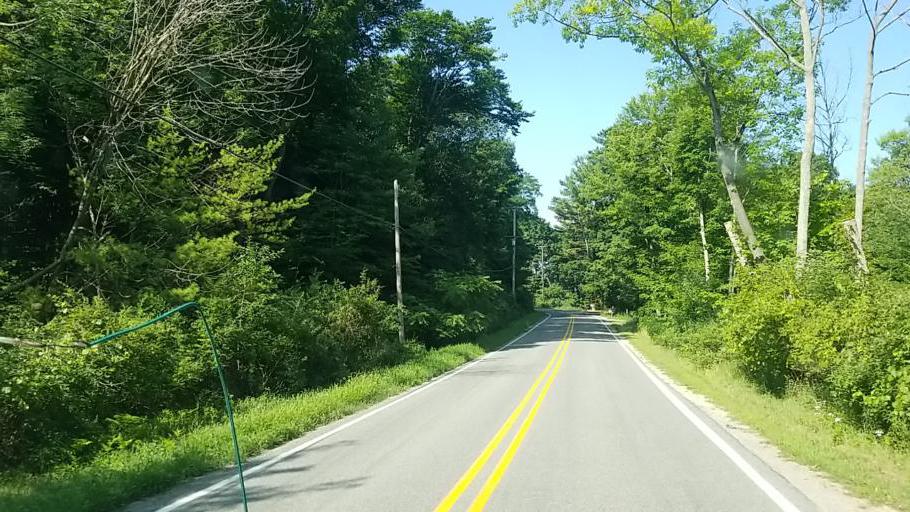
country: US
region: Michigan
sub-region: Muskegon County
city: Whitehall
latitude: 43.3744
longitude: -86.3744
